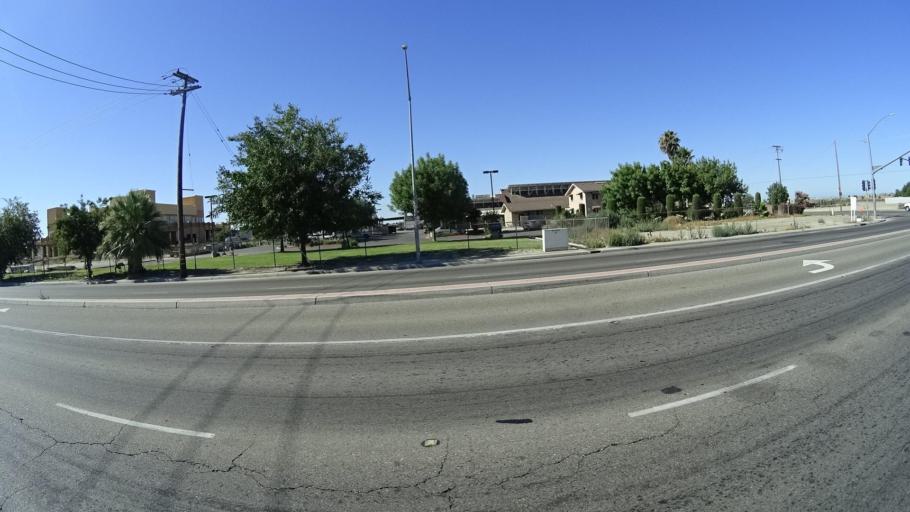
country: US
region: California
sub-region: Fresno County
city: Easton
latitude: 36.6923
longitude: -119.7810
